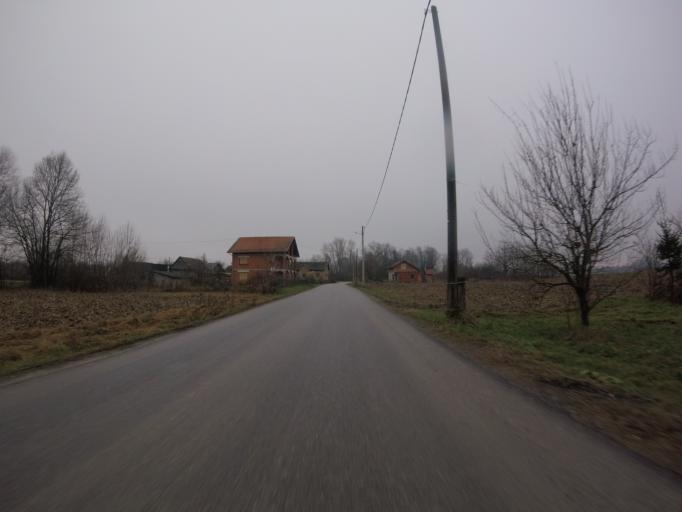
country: HR
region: Sisacko-Moslavacka
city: Lekenik
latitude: 45.6334
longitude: 16.2841
